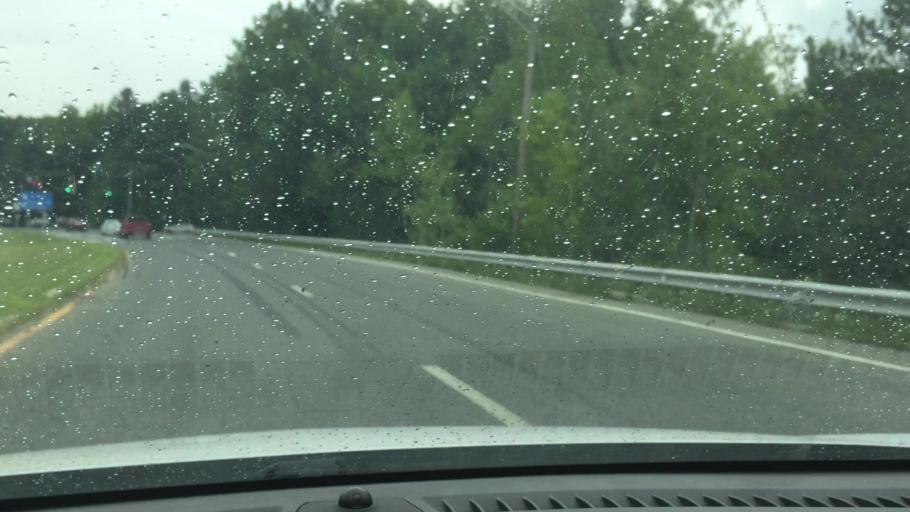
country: US
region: Massachusetts
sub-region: Berkshire County
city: Lenox
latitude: 42.3371
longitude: -73.2825
